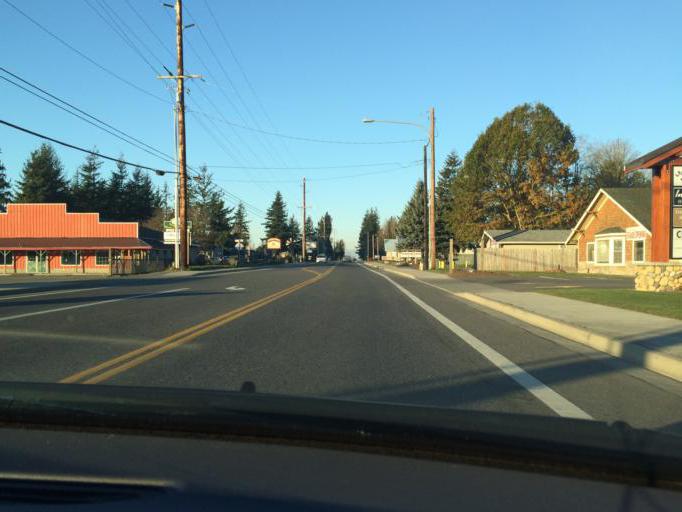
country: US
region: Washington
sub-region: Whatcom County
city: Lynden
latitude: 48.8923
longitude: -122.4424
